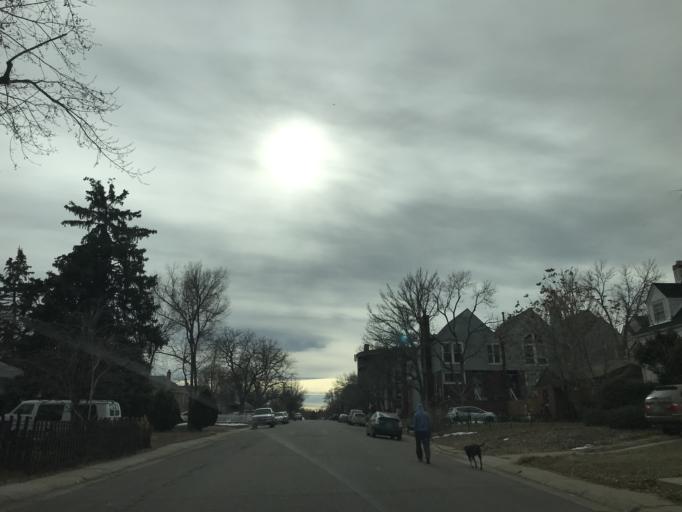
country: US
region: Colorado
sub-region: Arapahoe County
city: Glendale
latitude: 39.7333
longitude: -104.9184
